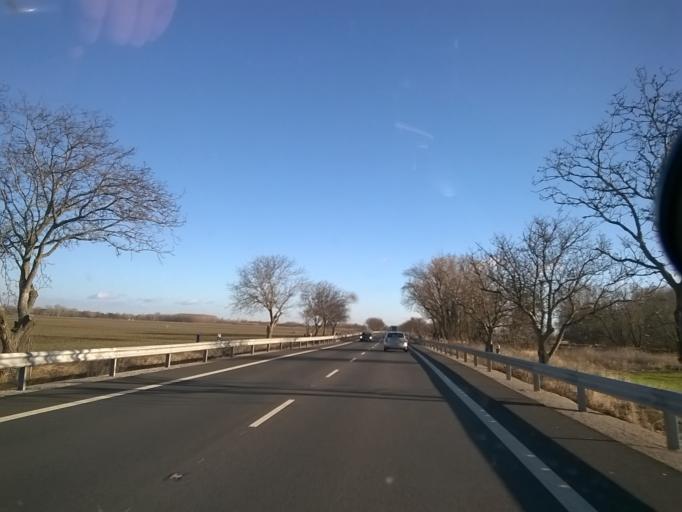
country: SK
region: Trnavsky
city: Sladkovicovo
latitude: 48.2008
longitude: 17.5596
